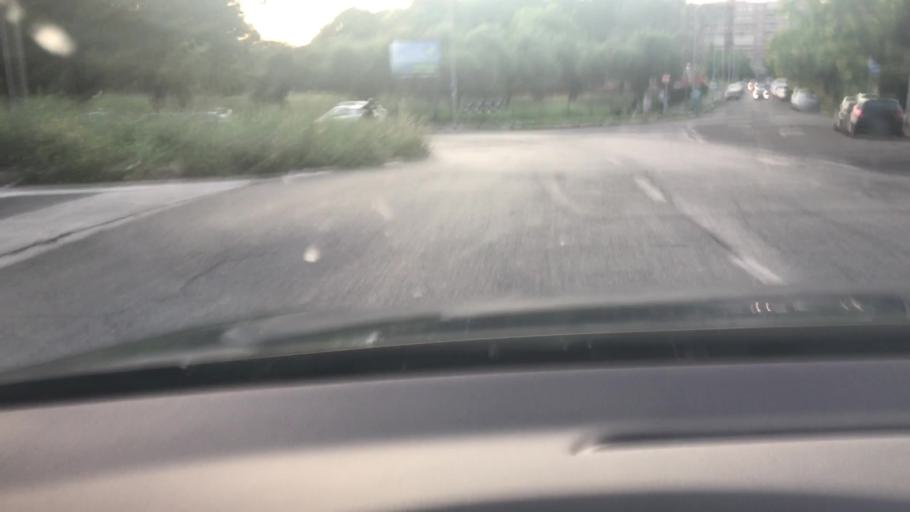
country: IT
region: Latium
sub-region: Citta metropolitana di Roma Capitale
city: Rome
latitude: 41.9328
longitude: 12.5578
